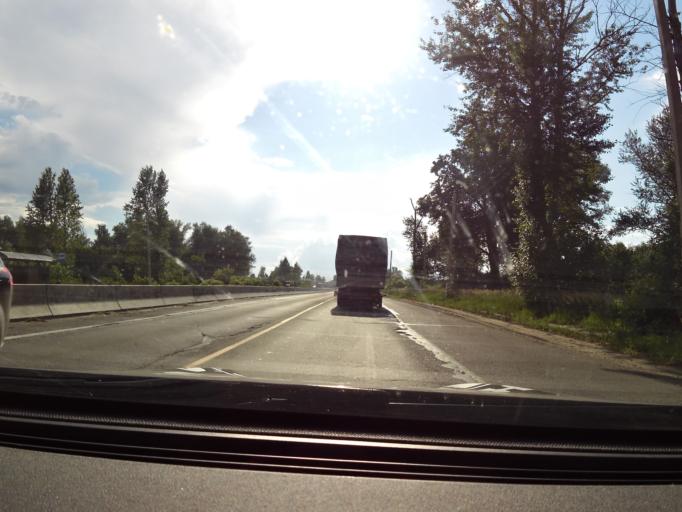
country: RU
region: Nizjnij Novgorod
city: Mulino
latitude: 56.2766
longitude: 42.9806
